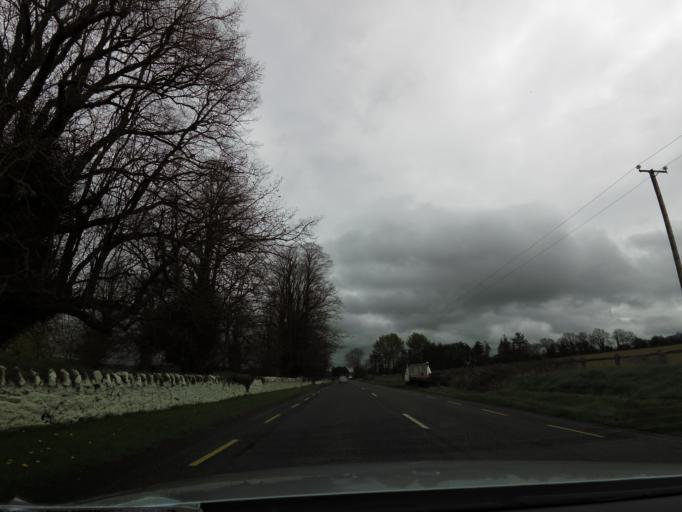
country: IE
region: Leinster
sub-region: Kilkenny
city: Ballyragget
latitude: 52.7235
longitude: -7.3571
